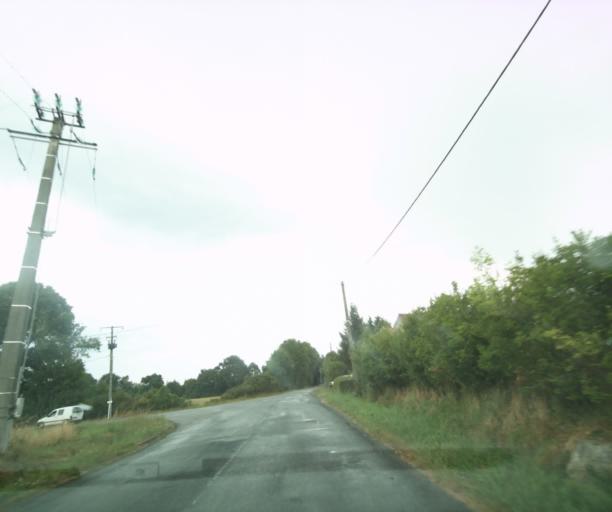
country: FR
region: Poitou-Charentes
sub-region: Departement de la Charente-Maritime
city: Tonnay-Charente
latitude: 45.9409
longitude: -0.8739
